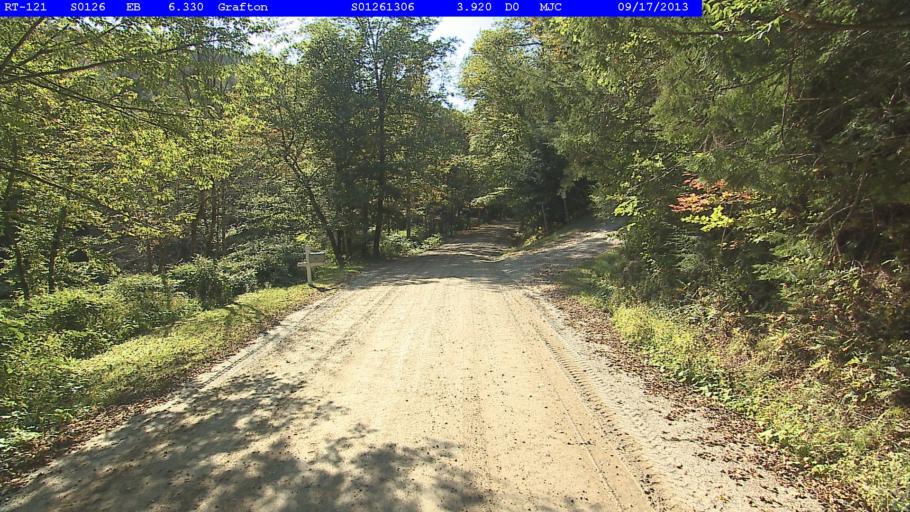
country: US
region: Vermont
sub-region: Windsor County
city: Chester
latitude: 43.1929
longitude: -72.6176
